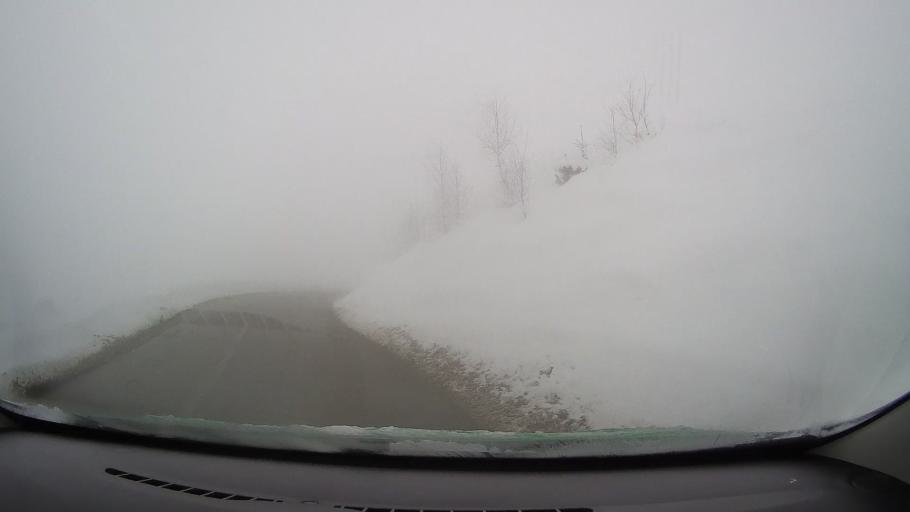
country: RO
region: Sibiu
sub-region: Comuna Poiana Sibiului
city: Poiana Sibiului
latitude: 45.7978
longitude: 23.7091
